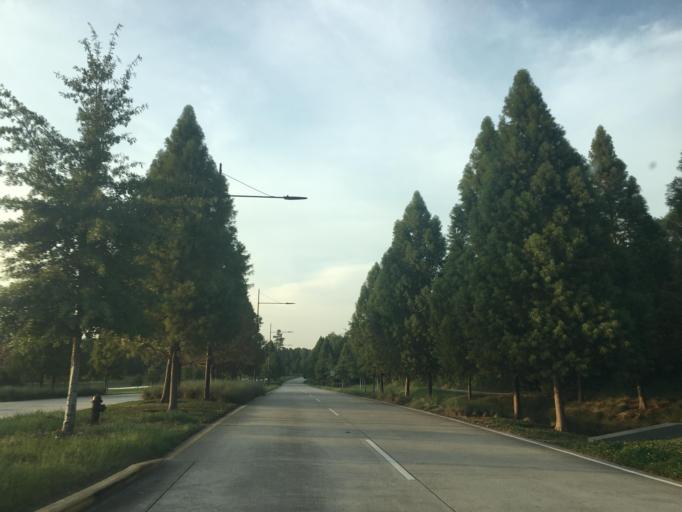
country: US
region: Texas
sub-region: Harris County
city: Spring
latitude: 30.0990
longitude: -95.4385
